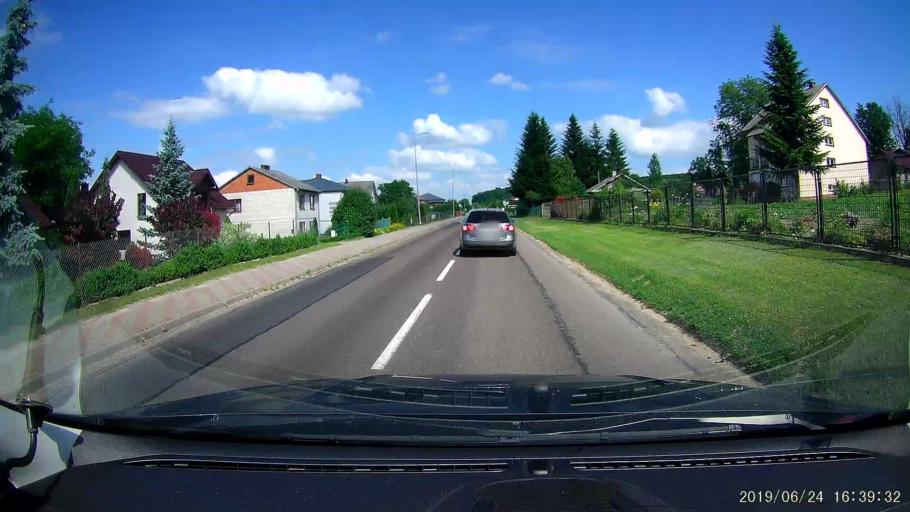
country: PL
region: Lublin Voivodeship
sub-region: Powiat tomaszowski
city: Rachanie
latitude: 50.5297
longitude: 23.5567
